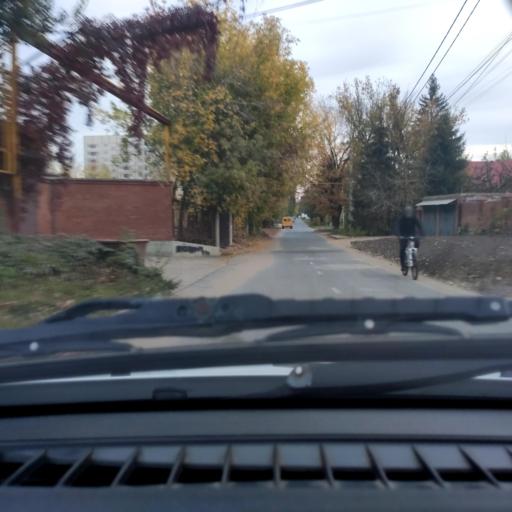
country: RU
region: Samara
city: Tol'yatti
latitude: 53.5325
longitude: 49.3889
